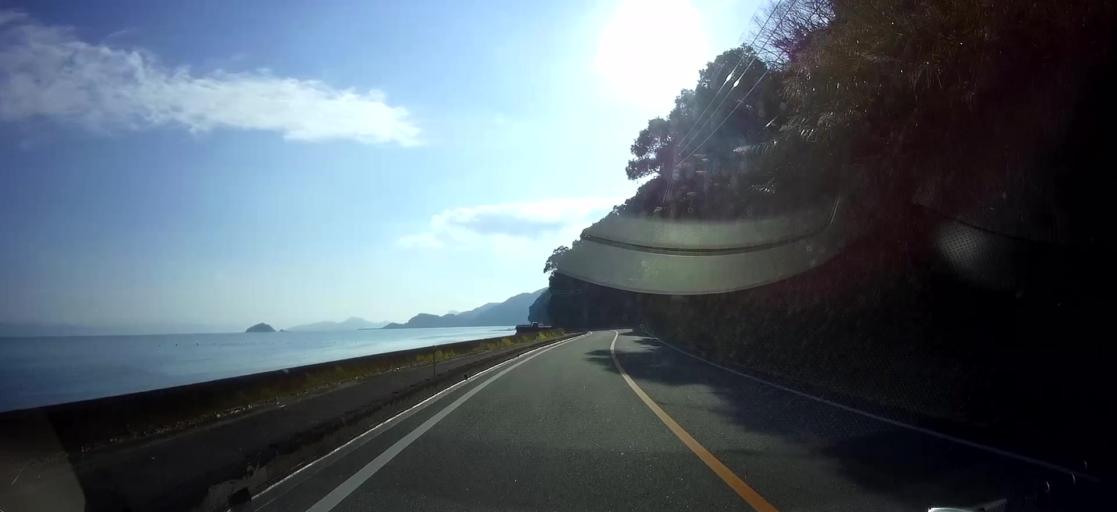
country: JP
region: Kumamoto
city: Yatsushiro
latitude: 32.4973
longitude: 130.4456
